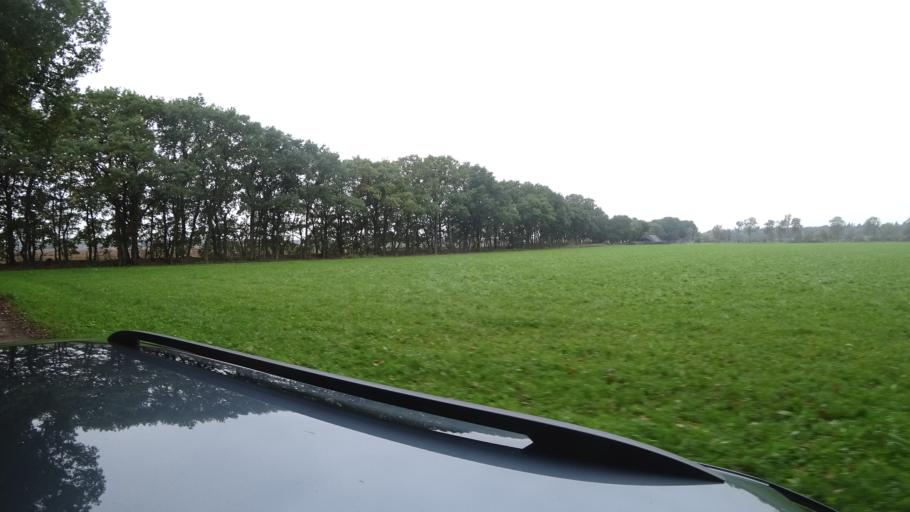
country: NL
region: Gelderland
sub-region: Gemeente Ede
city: Bennekom
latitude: 52.0443
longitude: 5.7234
